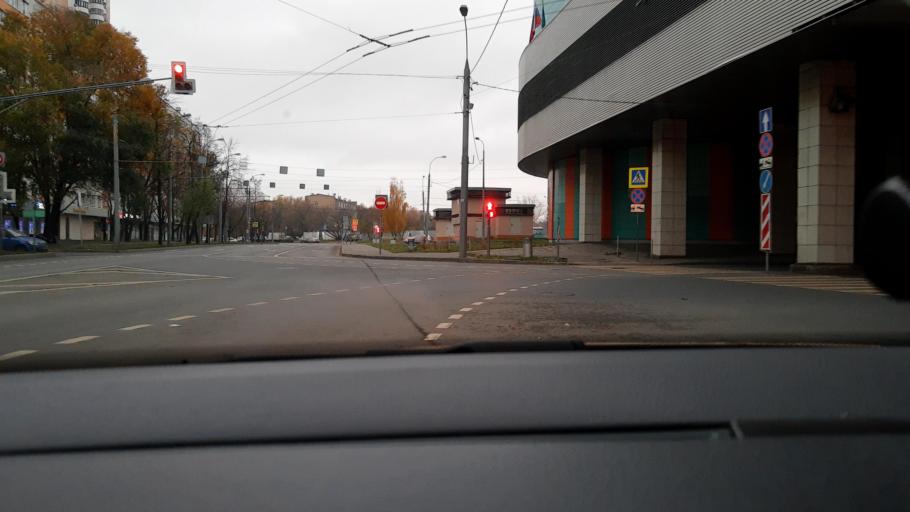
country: RU
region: Moscow
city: Khimki
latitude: 55.8630
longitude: 37.4344
